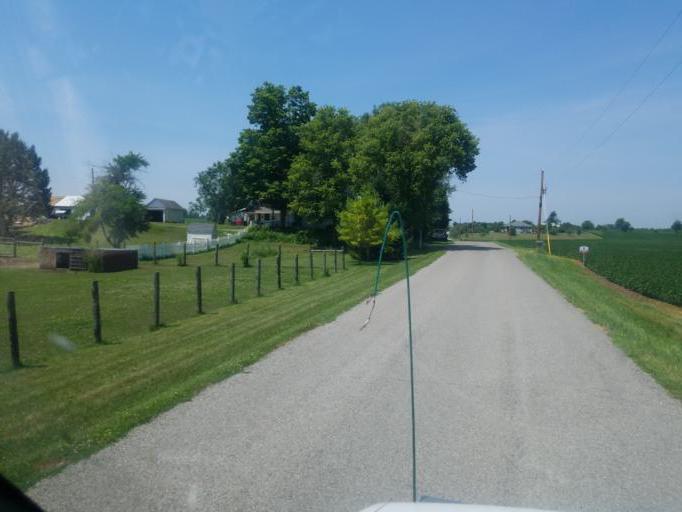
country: US
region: Ohio
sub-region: Logan County
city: West Liberty
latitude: 40.2921
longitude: -83.8240
